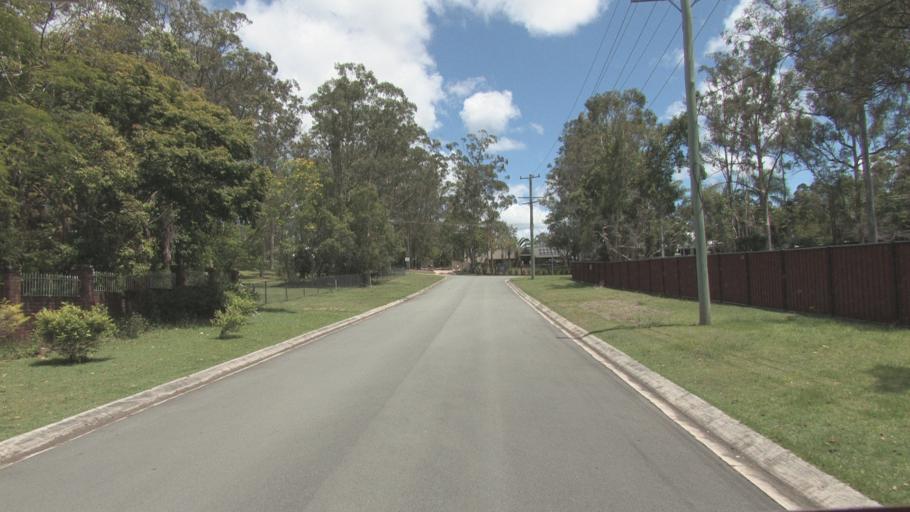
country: AU
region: Queensland
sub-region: Logan
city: Beenleigh
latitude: -27.6687
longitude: 153.2168
